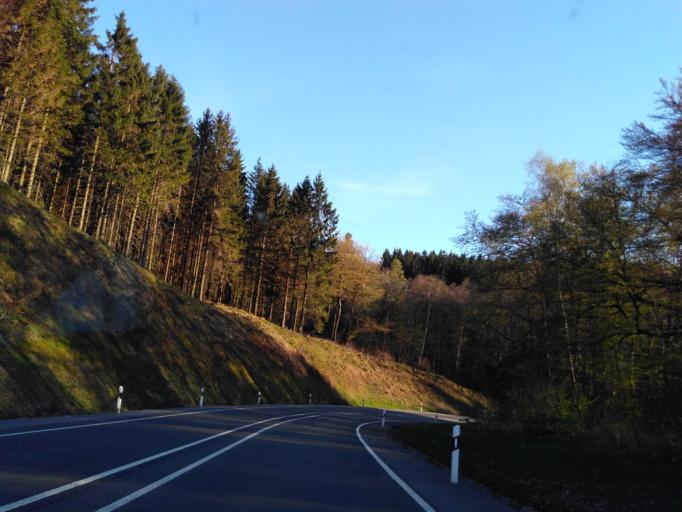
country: DE
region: North Rhine-Westphalia
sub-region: Regierungsbezirk Arnsberg
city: Herscheid
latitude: 51.1496
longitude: 7.7434
